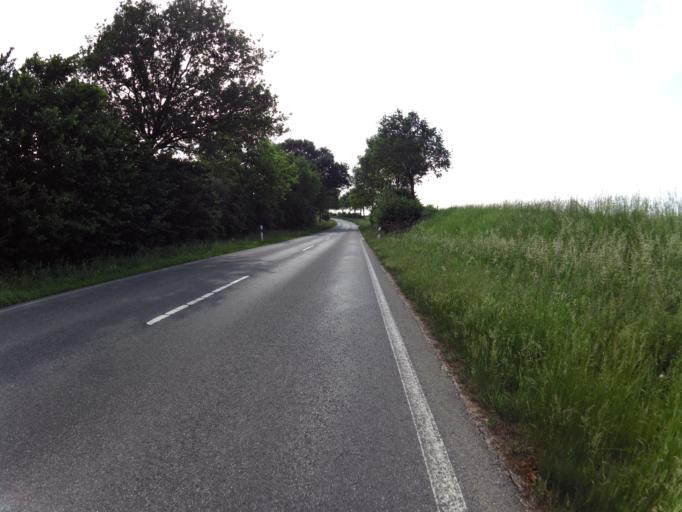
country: DE
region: North Rhine-Westphalia
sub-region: Regierungsbezirk Koln
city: Aldenhoven
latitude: 50.9338
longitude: 6.2796
